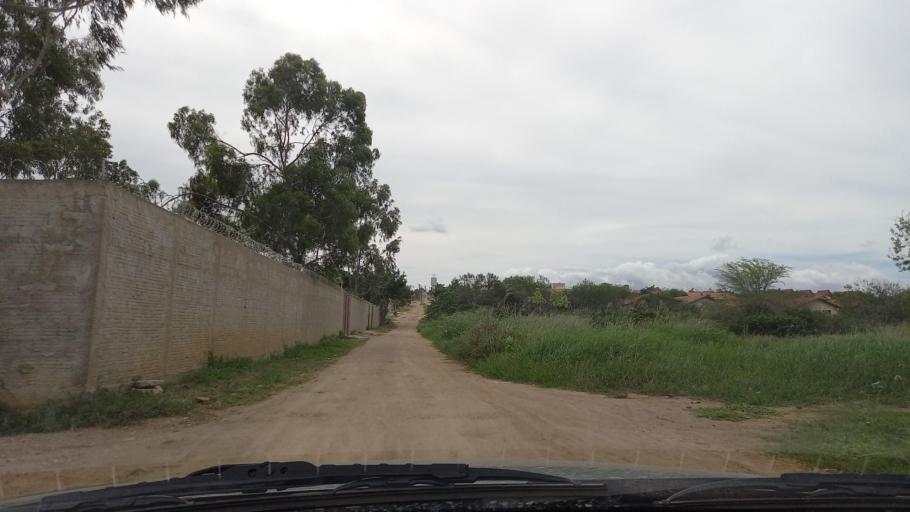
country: BR
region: Pernambuco
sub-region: Gravata
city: Gravata
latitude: -8.2008
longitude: -35.5937
